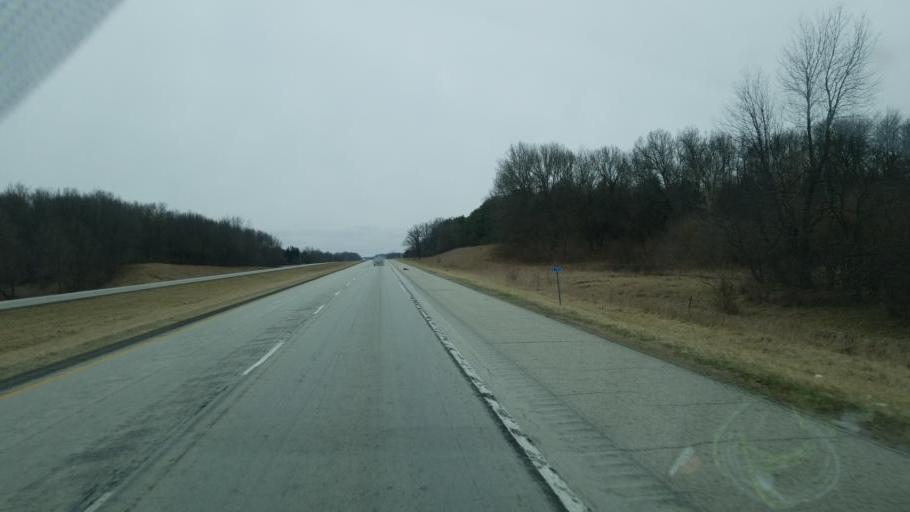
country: US
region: Indiana
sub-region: Fulton County
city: Rochester
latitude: 41.0730
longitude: -86.2401
